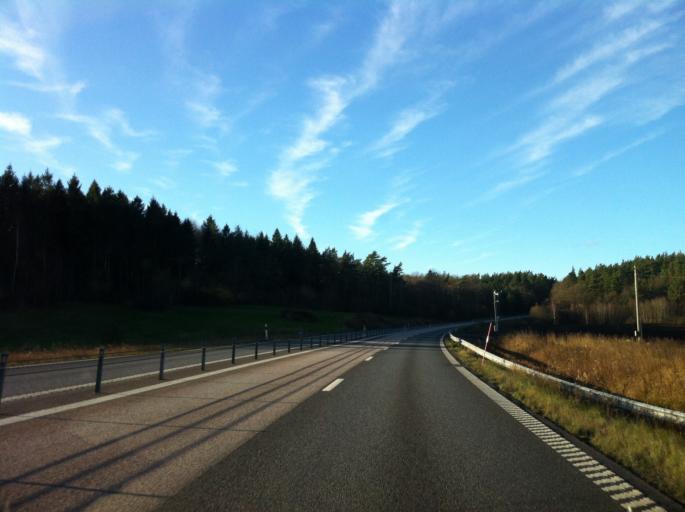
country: SE
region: Blekinge
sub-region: Karlshamns Kommun
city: Karlshamn
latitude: 56.1872
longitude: 14.9079
